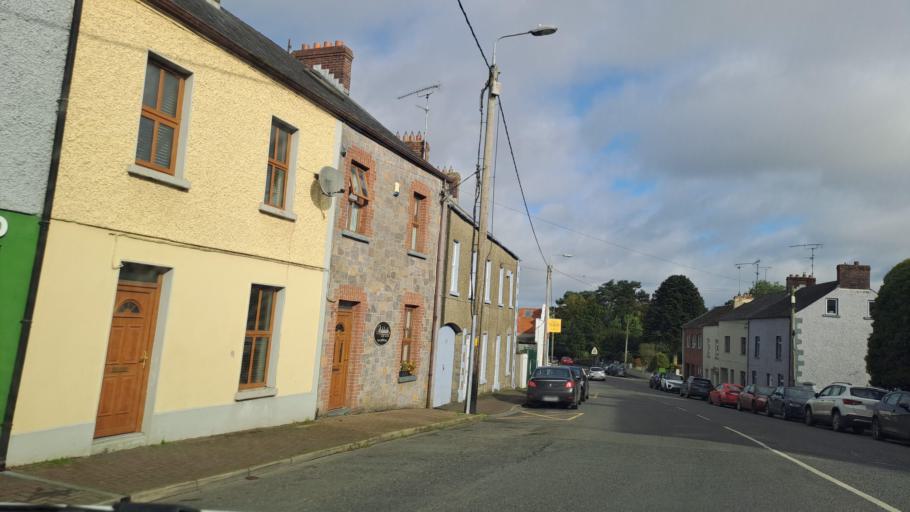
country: IE
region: Ulster
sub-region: An Cabhan
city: Bailieborough
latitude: 53.9175
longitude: -6.9722
